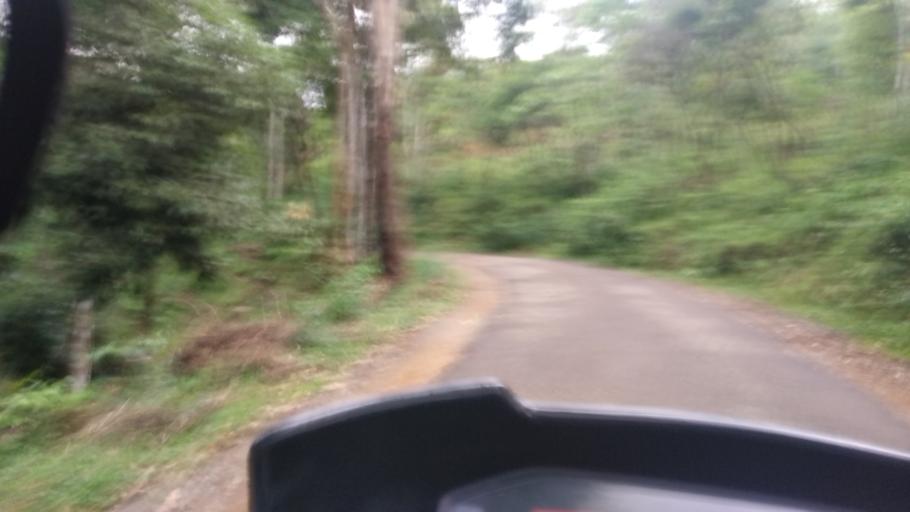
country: IN
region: Tamil Nadu
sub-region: Theni
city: Gudalur
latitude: 9.5498
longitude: 77.0561
